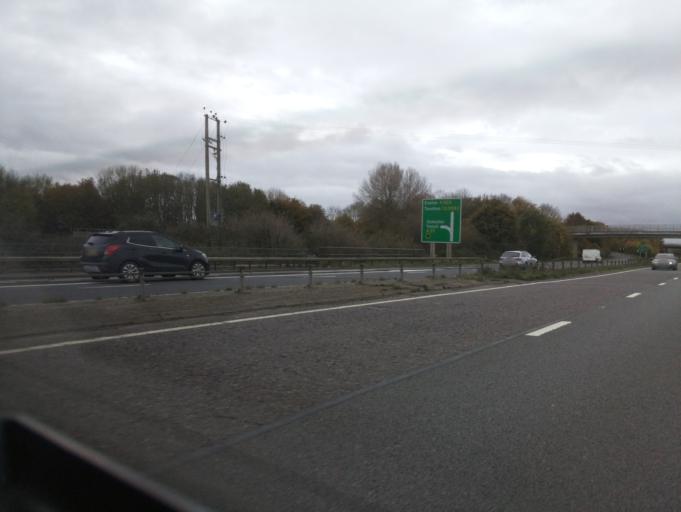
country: GB
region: England
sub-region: Somerset
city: Ilchester
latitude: 51.0028
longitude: -2.6923
